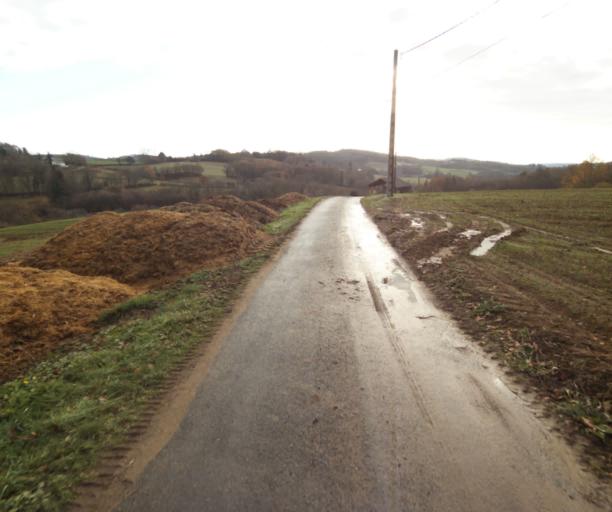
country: FR
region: Limousin
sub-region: Departement de la Correze
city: Saint-Mexant
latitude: 45.2528
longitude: 1.6385
